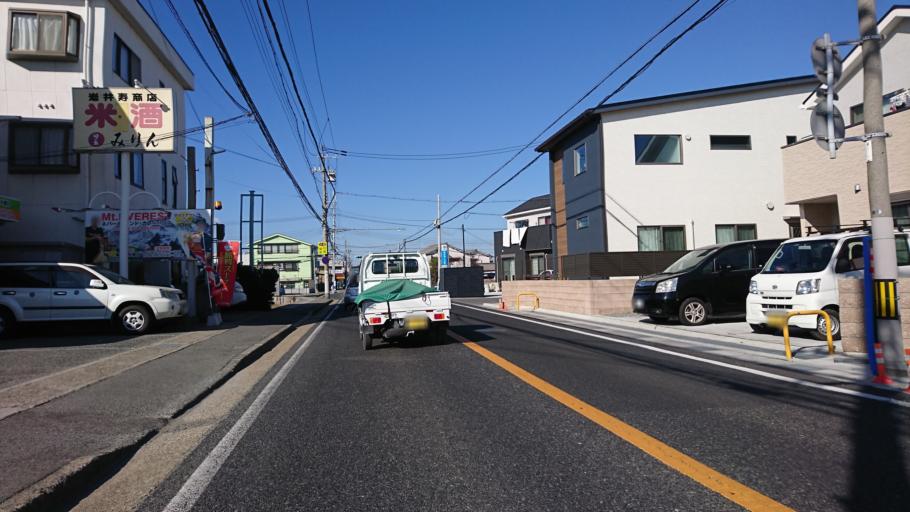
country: JP
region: Hyogo
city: Akashi
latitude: 34.6558
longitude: 134.9574
